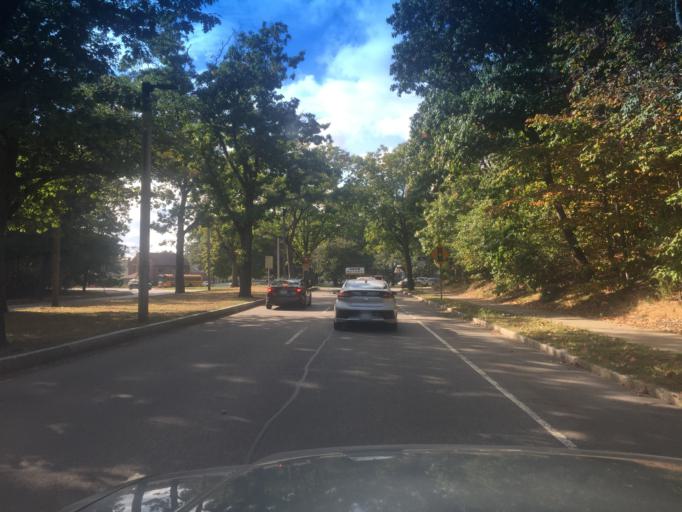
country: US
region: Massachusetts
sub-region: Suffolk County
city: Jamaica Plain
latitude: 42.2964
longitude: -71.1441
